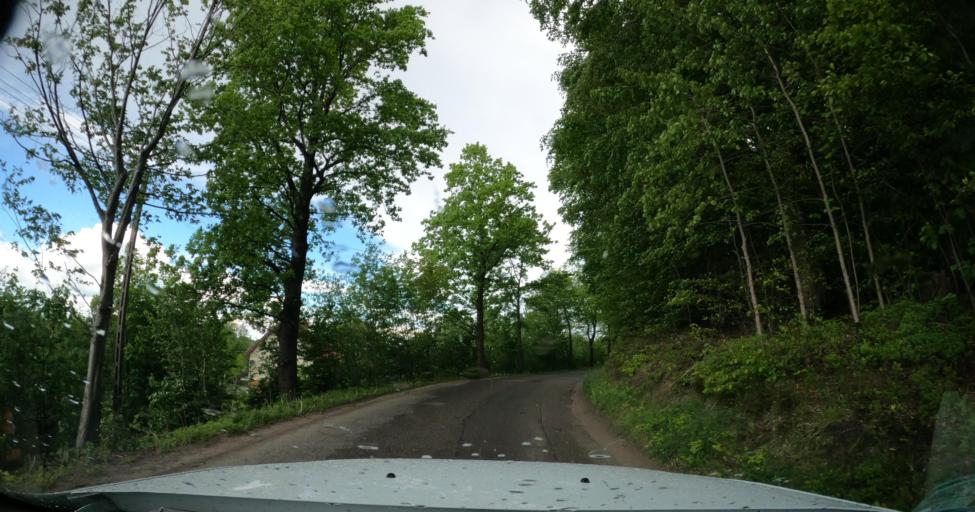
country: PL
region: Pomeranian Voivodeship
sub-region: Powiat kartuski
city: Garcz
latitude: 54.3439
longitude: 18.1462
